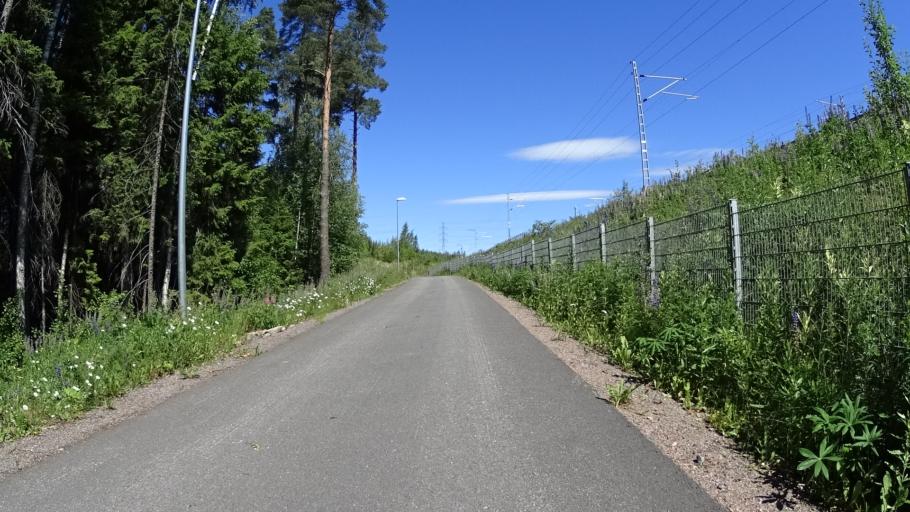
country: FI
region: Uusimaa
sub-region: Helsinki
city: Kilo
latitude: 60.3069
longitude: 24.8413
